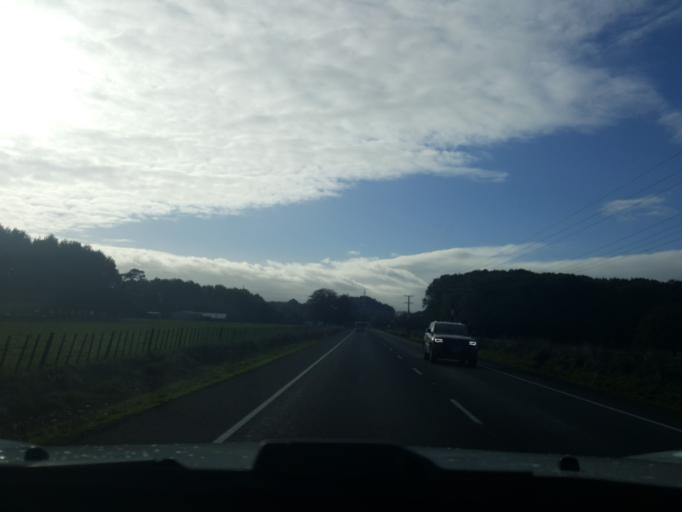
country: NZ
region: Waikato
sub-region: Waipa District
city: Cambridge
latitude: -37.6670
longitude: 175.4914
